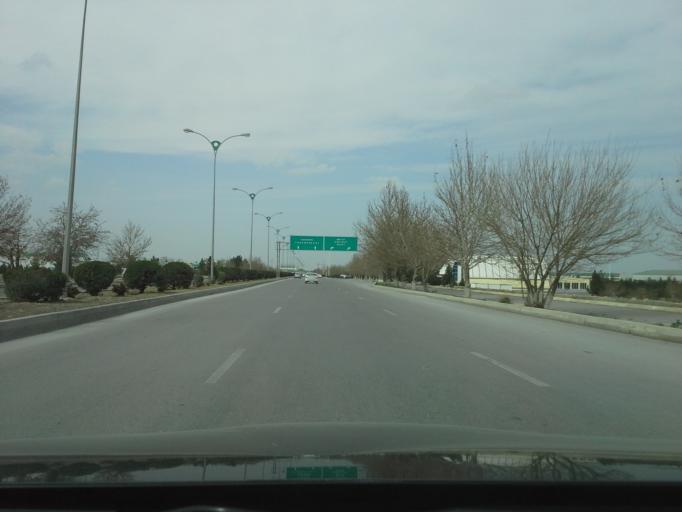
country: TM
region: Ahal
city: Abadan
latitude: 38.0486
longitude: 58.1865
